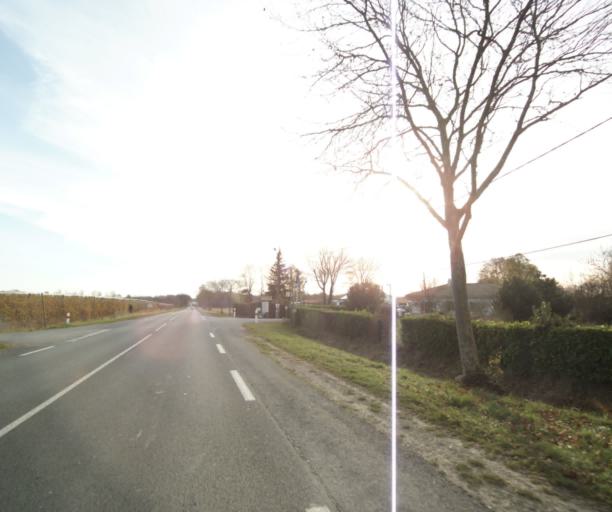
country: FR
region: Poitou-Charentes
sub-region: Departement de la Charente-Maritime
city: Fontcouverte
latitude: 45.7885
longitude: -0.5699
